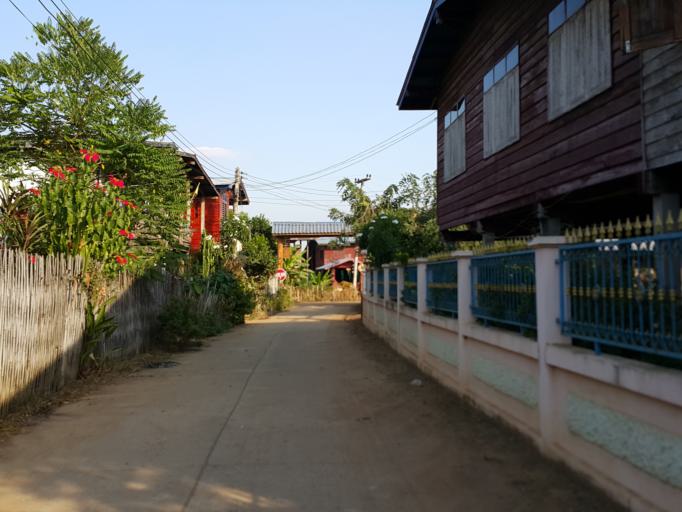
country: TH
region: Sukhothai
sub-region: Amphoe Si Satchanalai
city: Si Satchanalai
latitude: 17.4795
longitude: 99.6460
